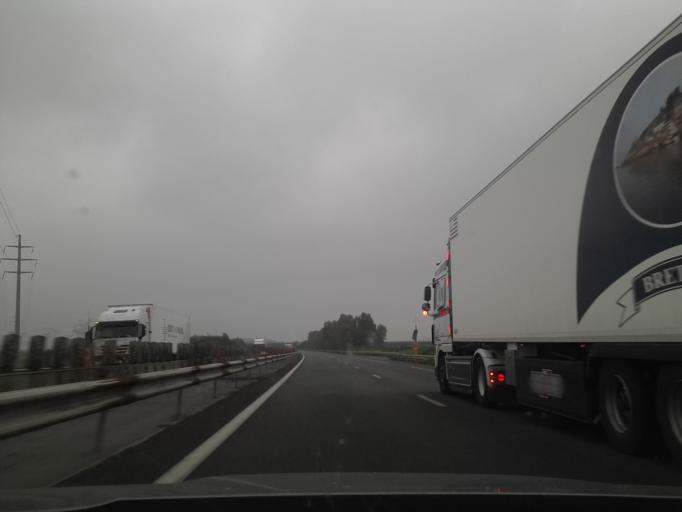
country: FR
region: Nord-Pas-de-Calais
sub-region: Departement du Nord
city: Escaudoeuvres
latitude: 50.2201
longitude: 3.2474
